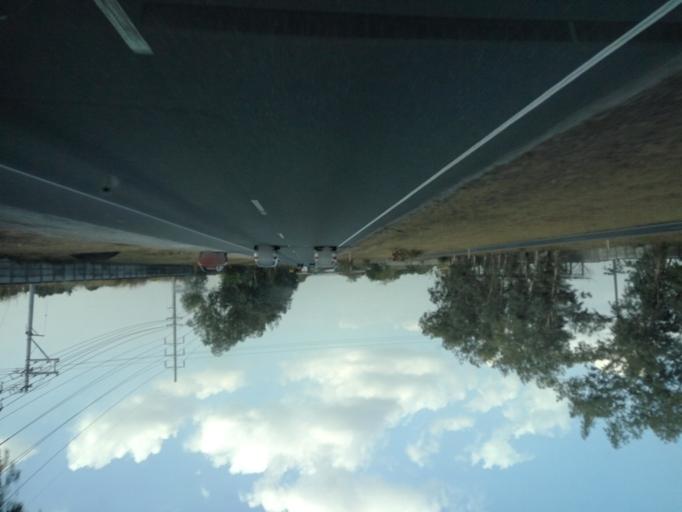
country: PH
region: Central Luzon
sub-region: Province of Pampanga
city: Culubasa
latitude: 15.1425
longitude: 120.6303
